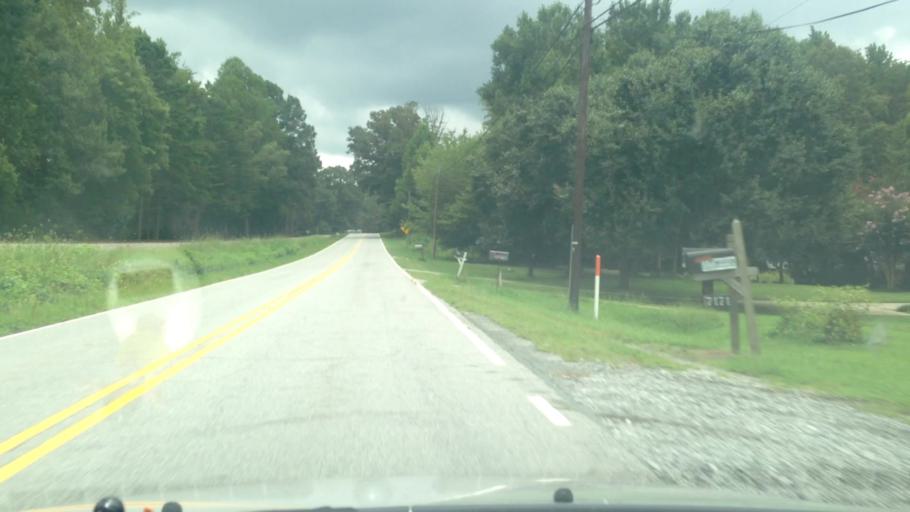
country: US
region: North Carolina
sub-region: Forsyth County
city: Walkertown
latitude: 36.2198
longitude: -80.1676
